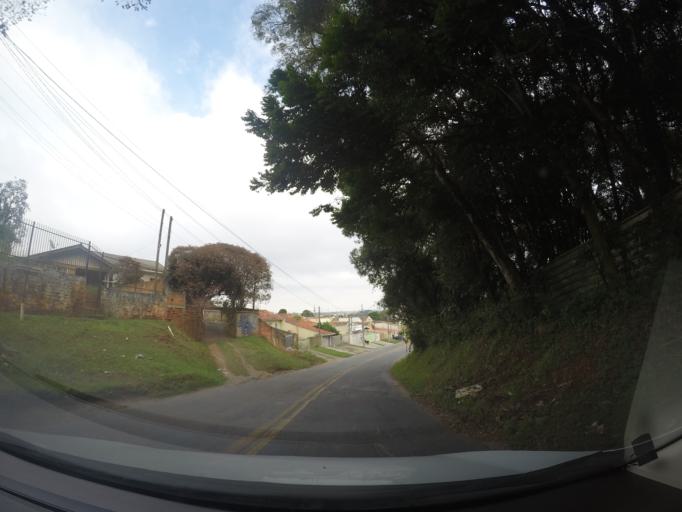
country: BR
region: Parana
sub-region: Colombo
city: Colombo
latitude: -25.3506
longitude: -49.2070
